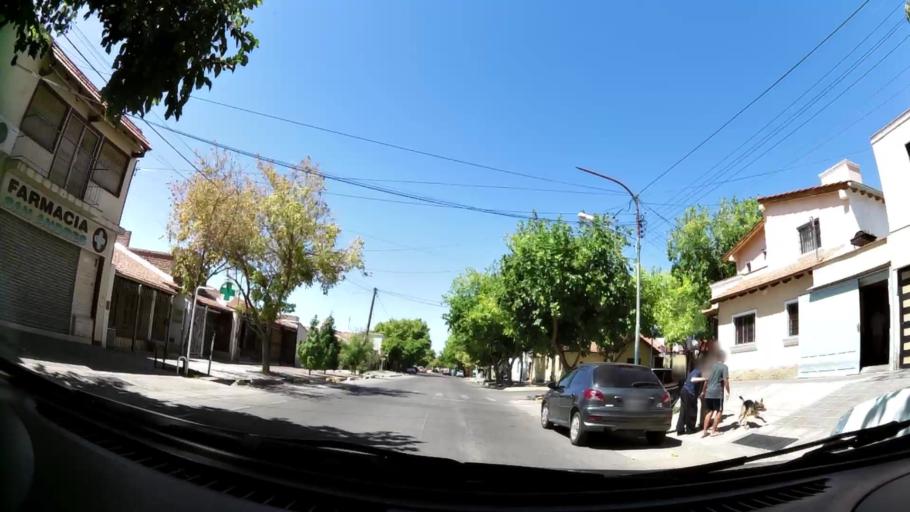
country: AR
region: Mendoza
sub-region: Departamento de Godoy Cruz
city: Godoy Cruz
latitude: -32.9466
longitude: -68.8631
